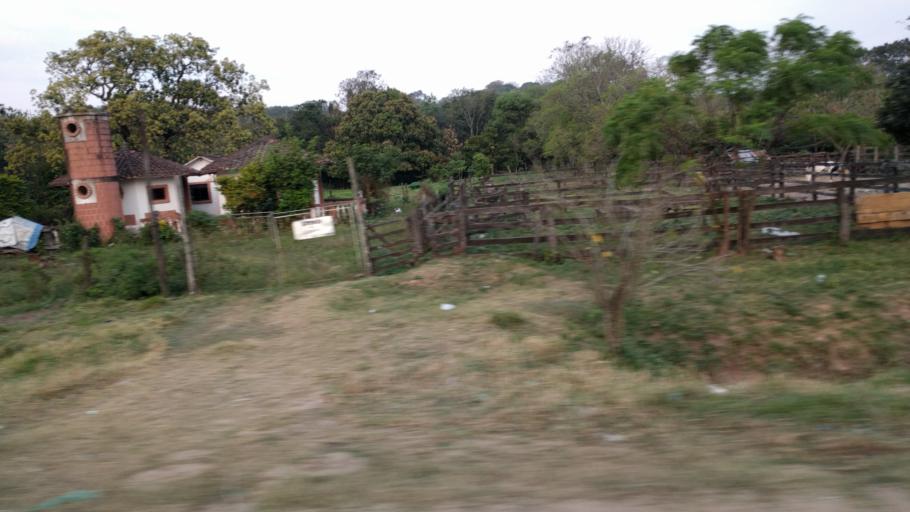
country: BO
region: Santa Cruz
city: Santa Rita
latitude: -17.9714
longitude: -63.3644
